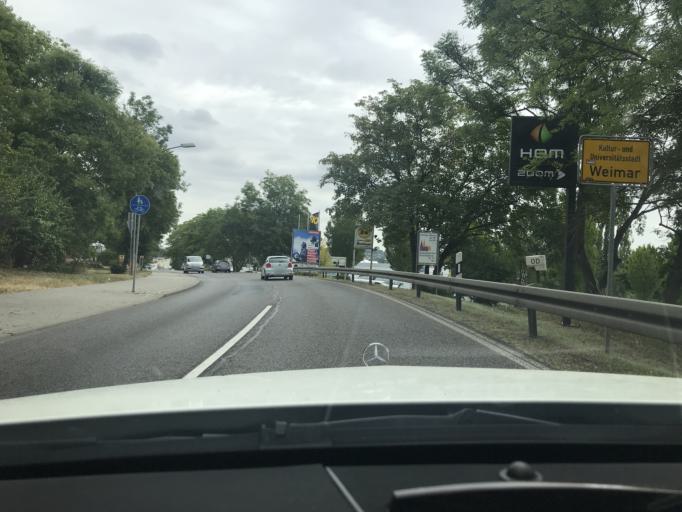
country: DE
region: Thuringia
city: Weimar
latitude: 50.9787
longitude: 11.3016
